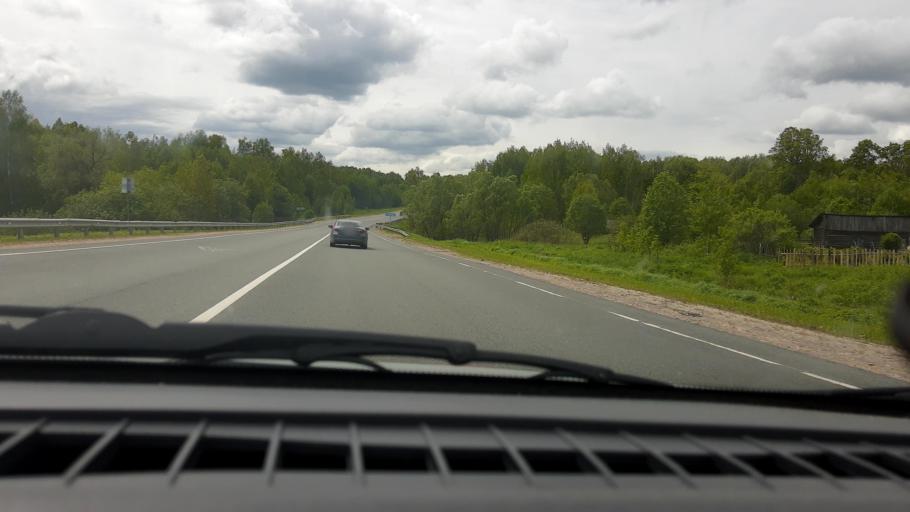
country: RU
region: Nizjnij Novgorod
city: Vladimirskoye
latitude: 56.9125
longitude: 45.0482
